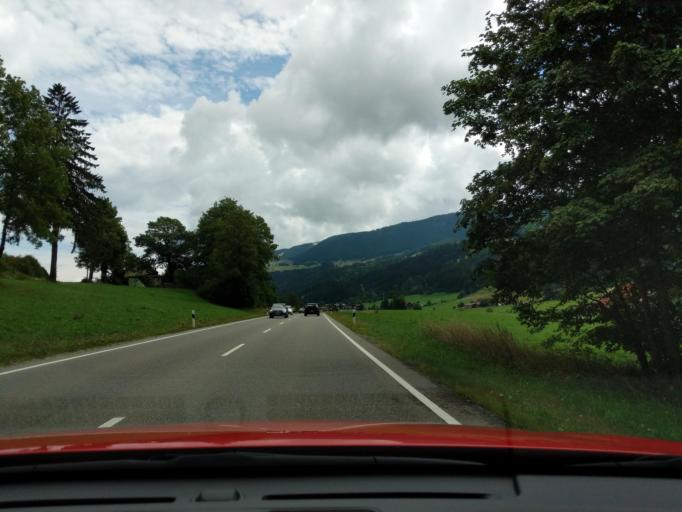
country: DE
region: Bavaria
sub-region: Swabia
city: Oberstaufen
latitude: 47.5546
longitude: 10.0671
